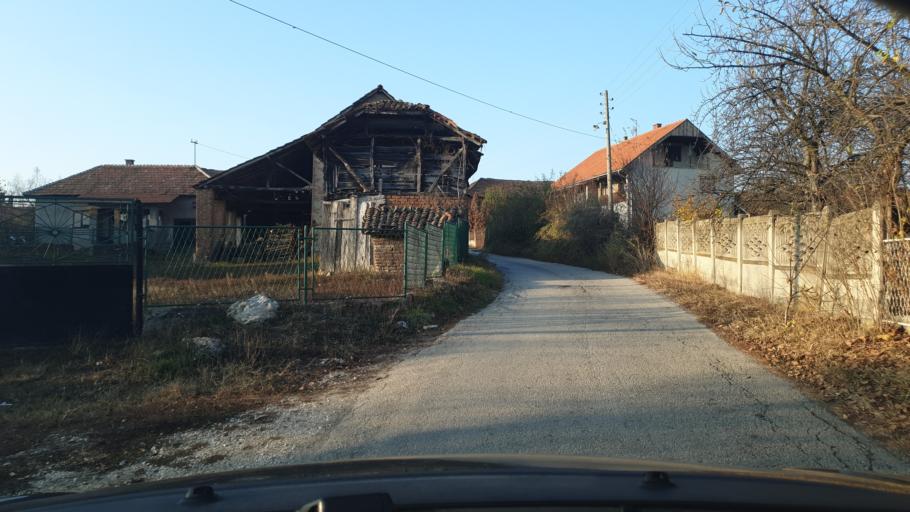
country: RS
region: Central Serbia
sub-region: Zajecarski Okrug
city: Zajecar
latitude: 44.0324
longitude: 22.3270
